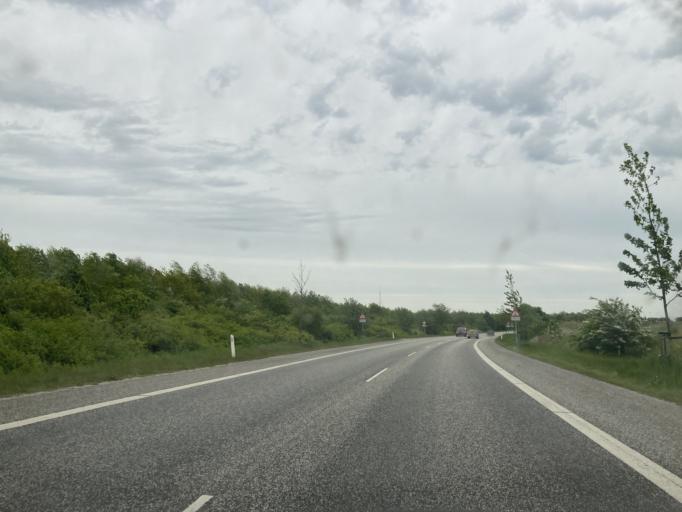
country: DK
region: Zealand
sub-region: Roskilde Kommune
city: Svogerslev
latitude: 55.6292
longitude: 12.0334
